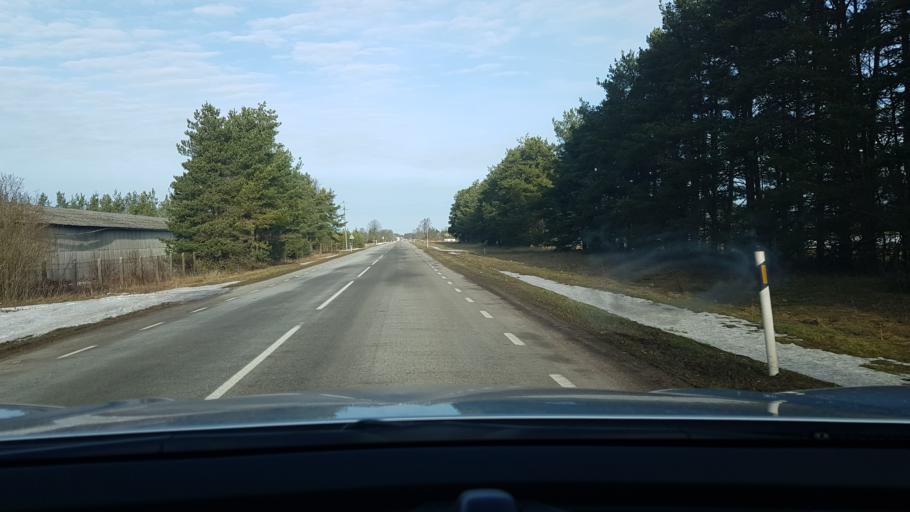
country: EE
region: Saare
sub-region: Kuressaare linn
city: Kuressaare
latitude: 58.5144
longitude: 22.7047
